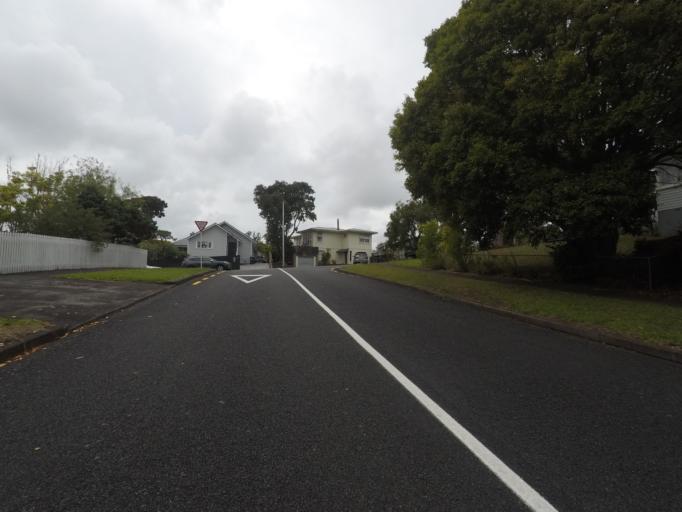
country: NZ
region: Auckland
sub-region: Auckland
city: Rosebank
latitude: -36.8863
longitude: 174.6756
